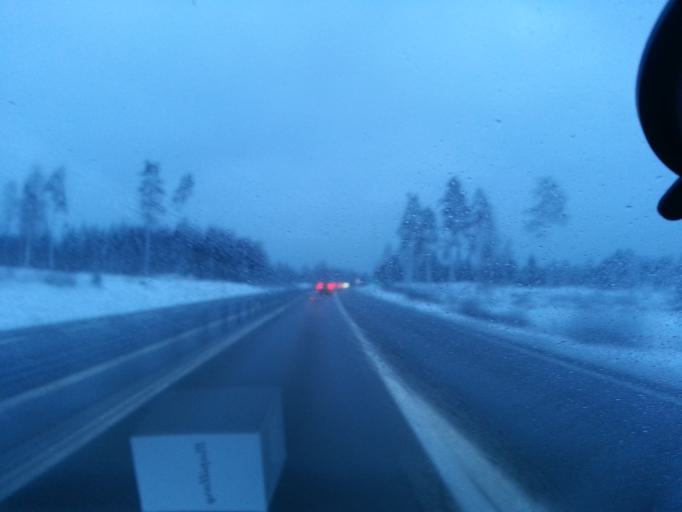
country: SE
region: Kronoberg
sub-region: Ljungby Kommun
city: Lagan
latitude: 56.9198
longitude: 13.9737
